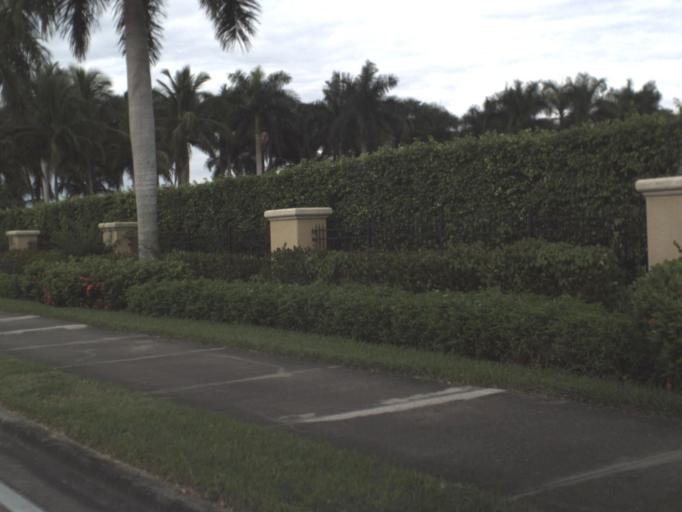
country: US
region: Florida
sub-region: Lee County
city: Harlem Heights
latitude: 26.5248
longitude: -81.9356
